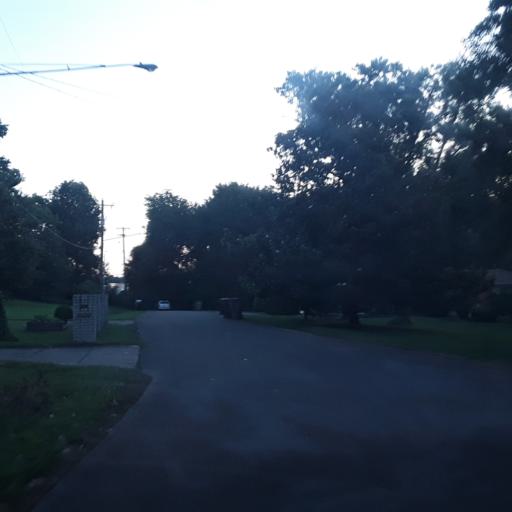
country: US
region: Tennessee
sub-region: Davidson County
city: Oak Hill
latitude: 36.0757
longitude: -86.7628
